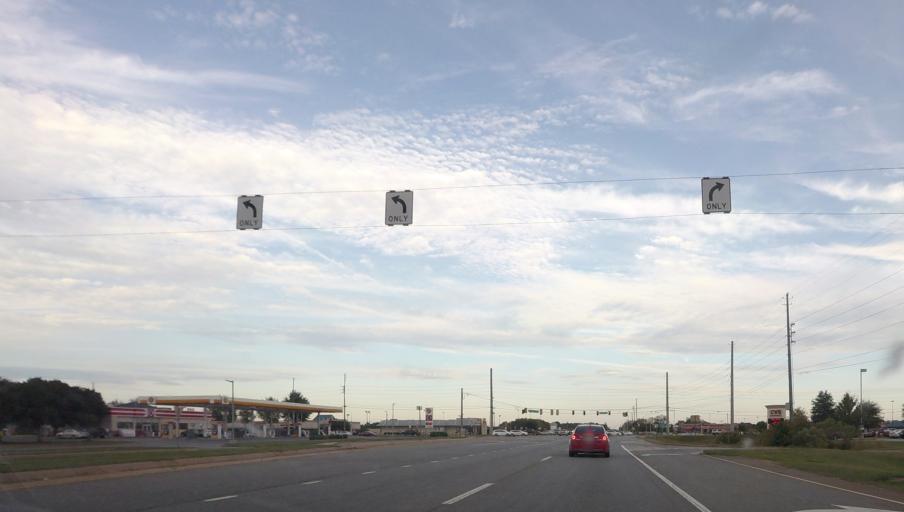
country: US
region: Georgia
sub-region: Houston County
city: Centerville
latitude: 32.5542
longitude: -83.6640
